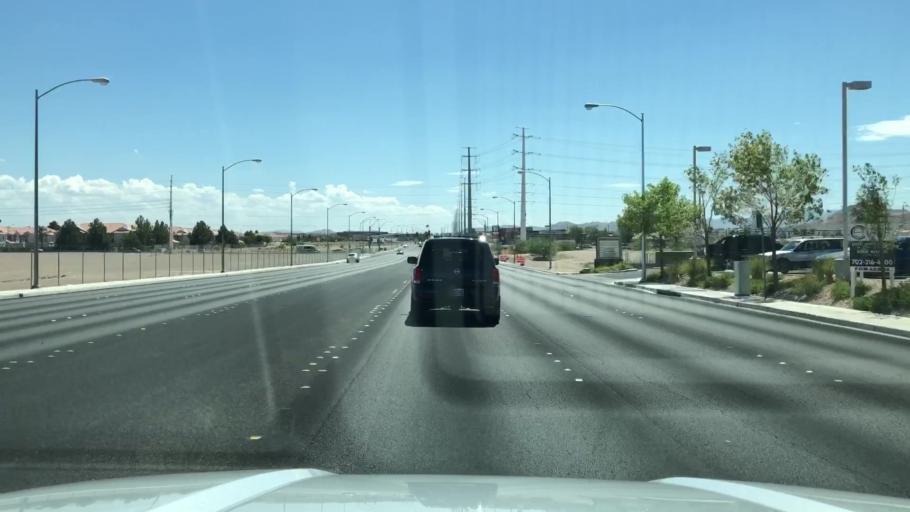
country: US
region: Nevada
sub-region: Clark County
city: Spring Valley
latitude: 36.0879
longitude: -115.2793
